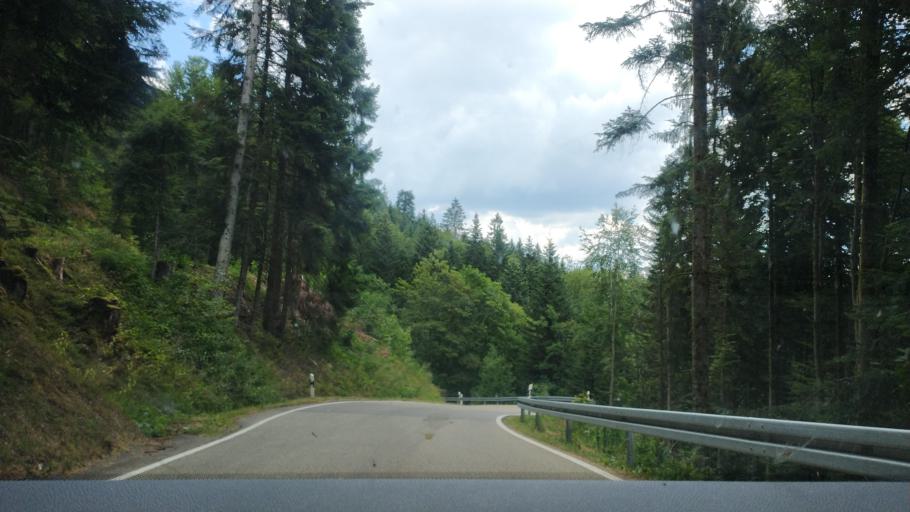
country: DE
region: Baden-Wuerttemberg
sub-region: Freiburg Region
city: Oppenau
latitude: 48.4255
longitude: 8.1582
